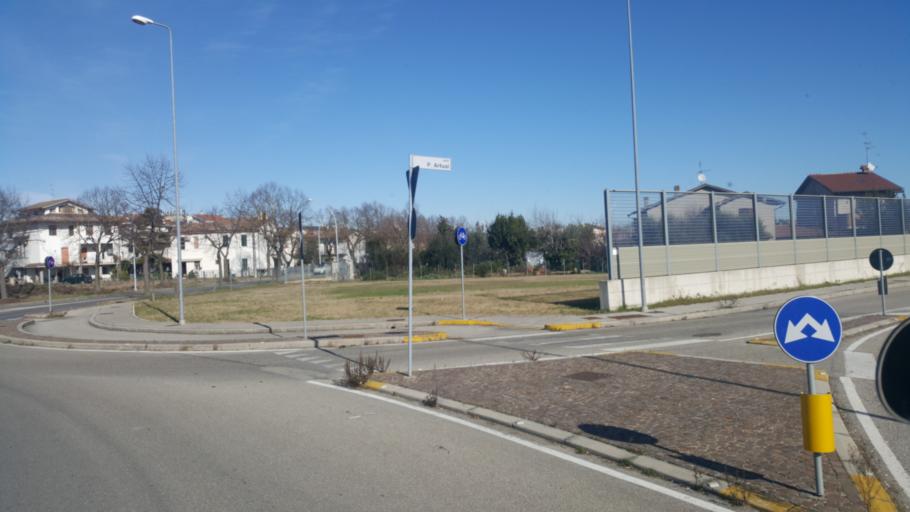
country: IT
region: Emilia-Romagna
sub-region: Forli-Cesena
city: Forli
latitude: 44.2446
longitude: 12.0795
